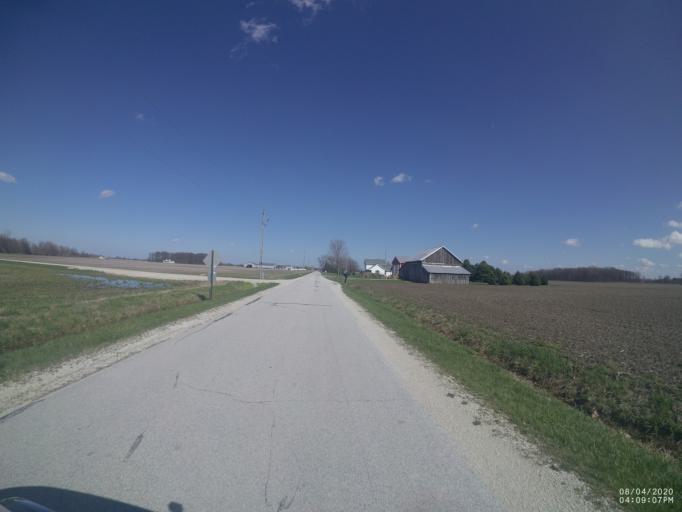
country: US
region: Ohio
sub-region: Sandusky County
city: Stony Prairie
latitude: 41.2899
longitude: -83.2139
